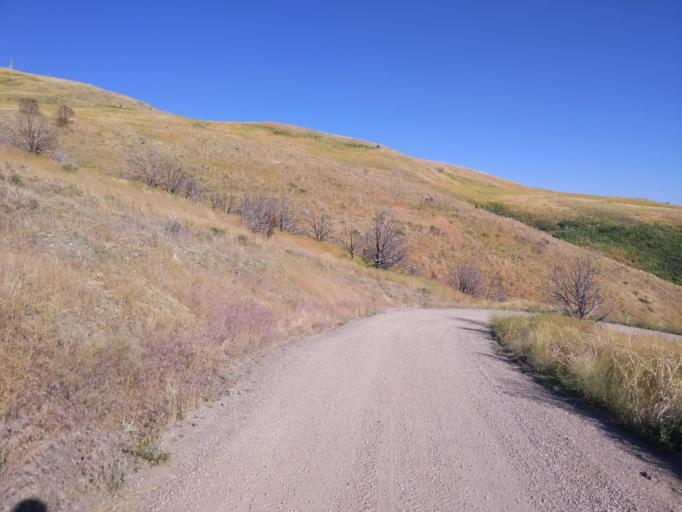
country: US
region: Idaho
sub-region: Bannock County
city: Pocatello
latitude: 42.8496
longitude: -112.3752
